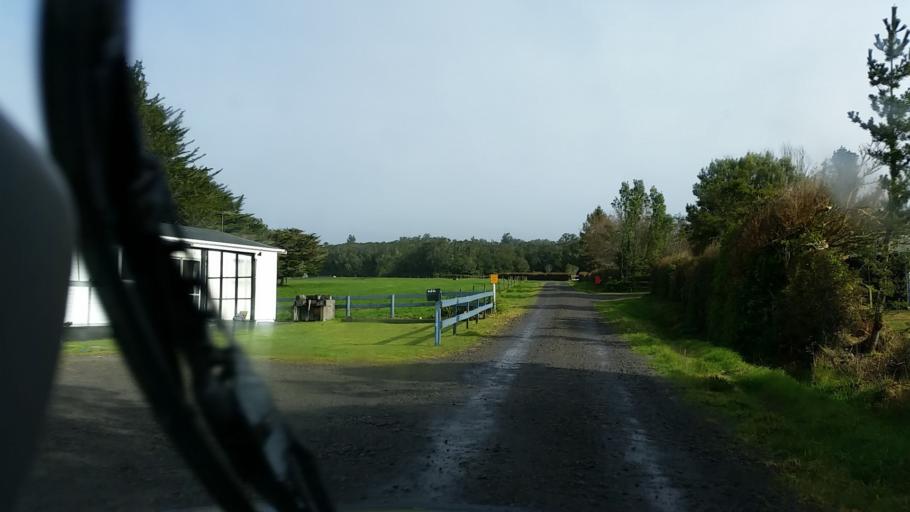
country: NZ
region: Taranaki
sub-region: South Taranaki District
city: Eltham
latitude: -39.2869
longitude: 174.1816
